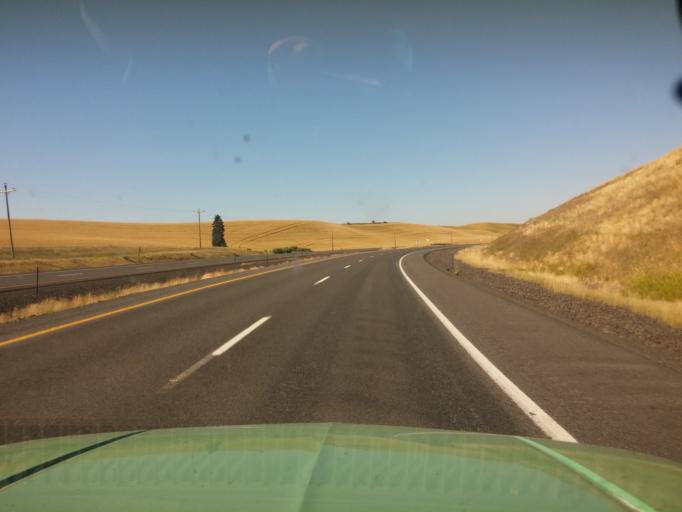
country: US
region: Idaho
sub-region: Nez Perce County
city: Lewiston
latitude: 46.4967
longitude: -117.0026
